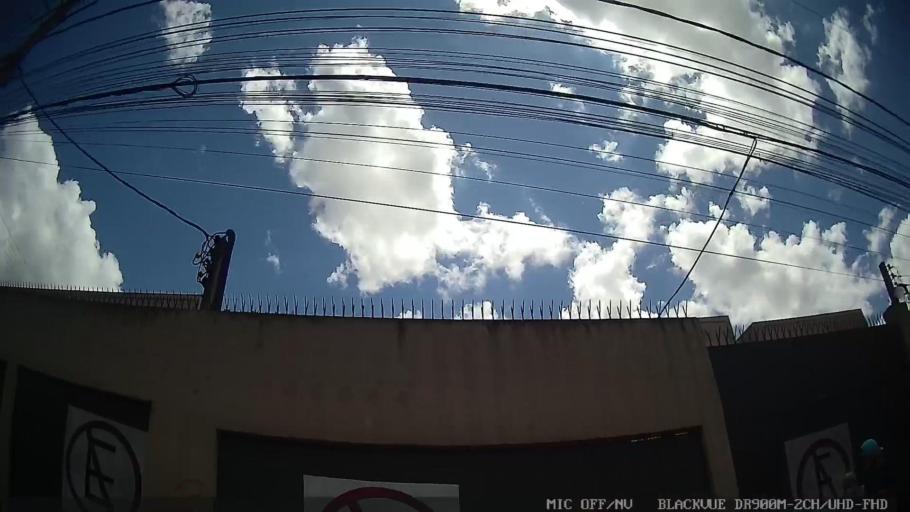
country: BR
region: Sao Paulo
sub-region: Diadema
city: Diadema
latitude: -23.6743
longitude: -46.6309
